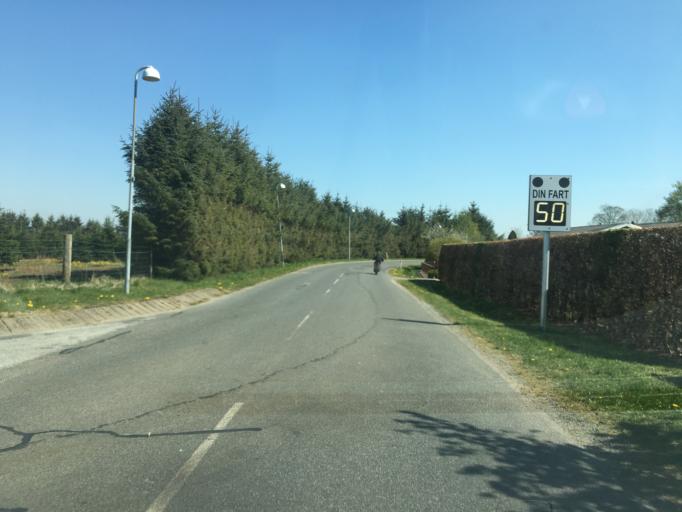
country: DK
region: South Denmark
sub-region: Aabenraa Kommune
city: Rodekro
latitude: 55.0341
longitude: 9.3019
